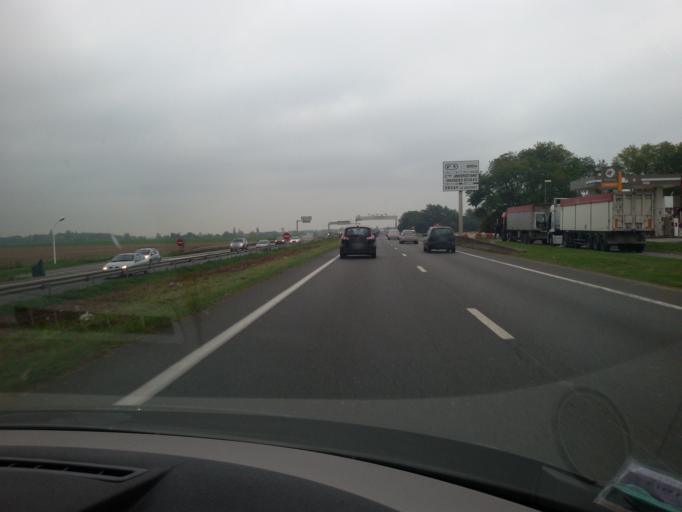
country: FR
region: Ile-de-France
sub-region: Departement de l'Essonne
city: Saclay
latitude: 48.7228
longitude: 2.1677
